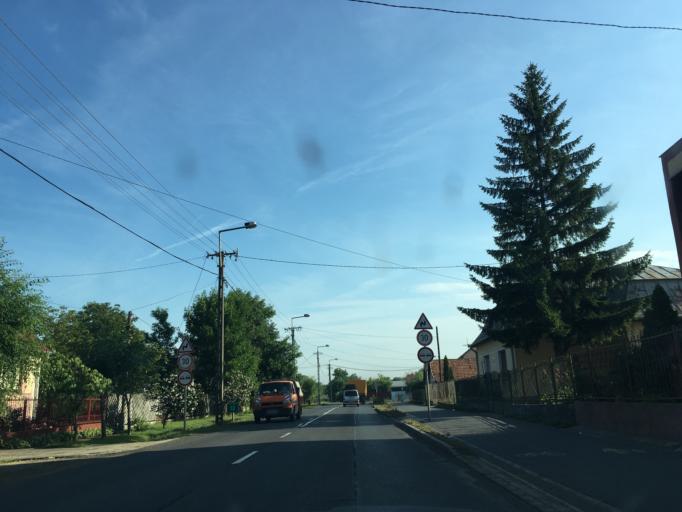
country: HU
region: Hajdu-Bihar
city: Hajdusamson
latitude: 47.6072
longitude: 21.7636
